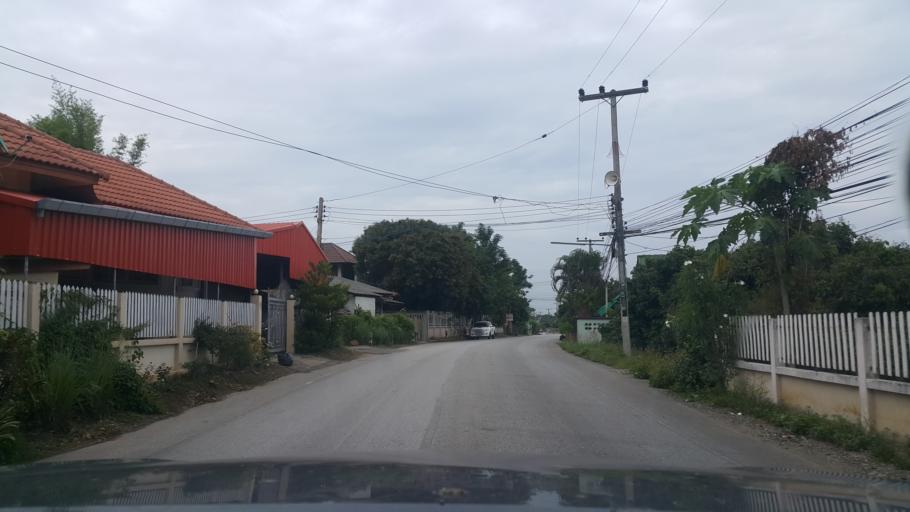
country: TH
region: Chiang Mai
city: San Pa Tong
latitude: 18.6526
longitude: 98.8373
